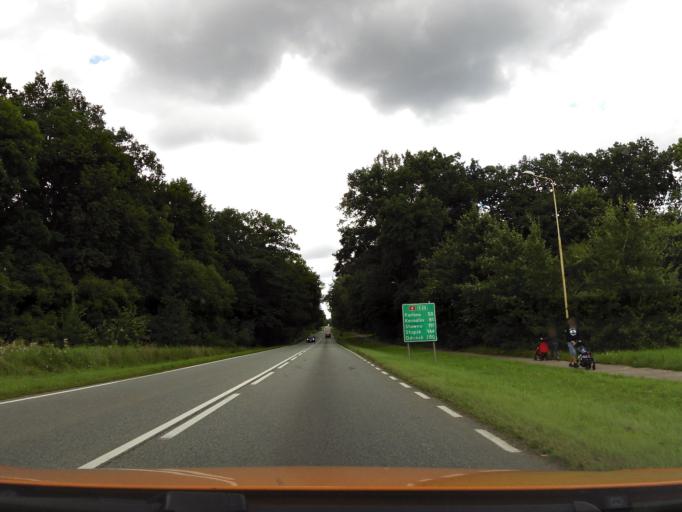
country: PL
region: West Pomeranian Voivodeship
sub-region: Powiat gryficki
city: Ploty
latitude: 53.8089
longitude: 15.2739
